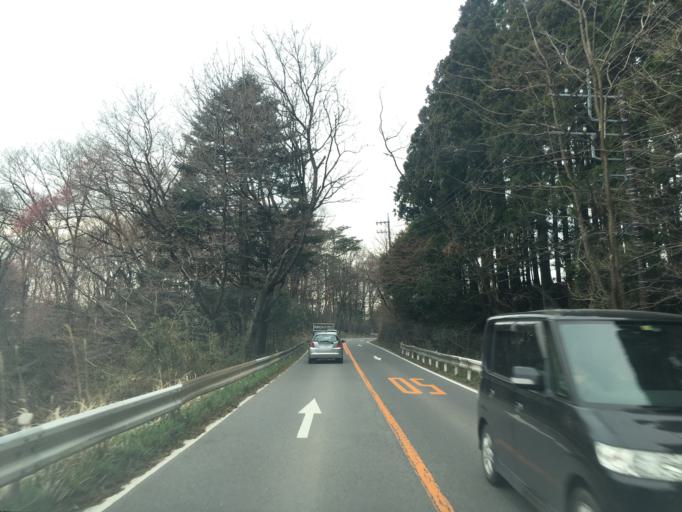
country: JP
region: Tochigi
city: Kuroiso
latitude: 36.9703
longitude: 139.9249
